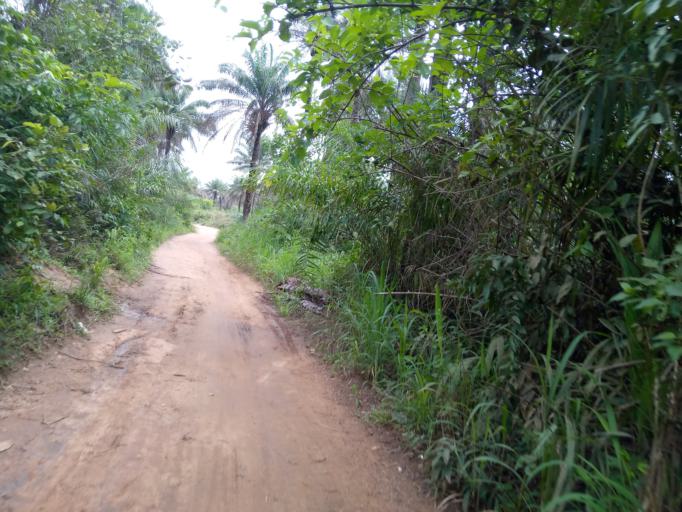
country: SL
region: Western Area
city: Waterloo
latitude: 8.3972
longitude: -12.9463
